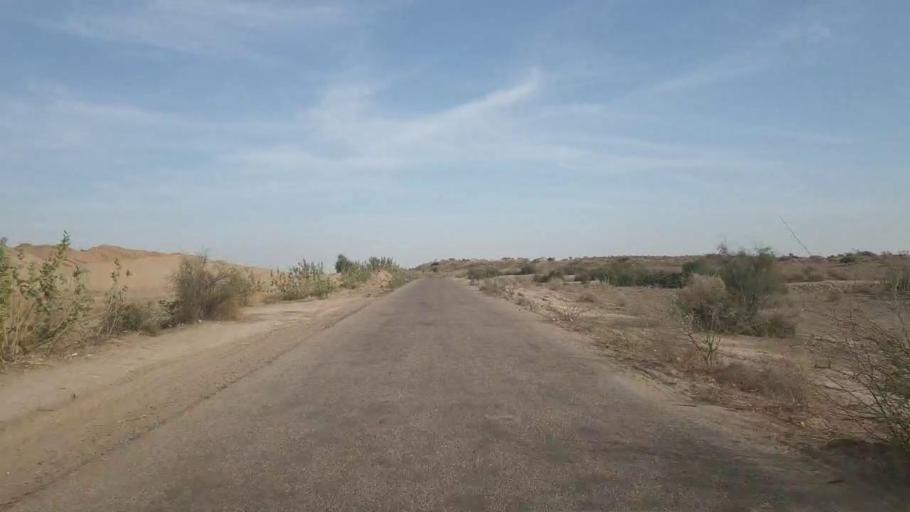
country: PK
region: Sindh
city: Nabisar
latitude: 25.0585
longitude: 69.6628
